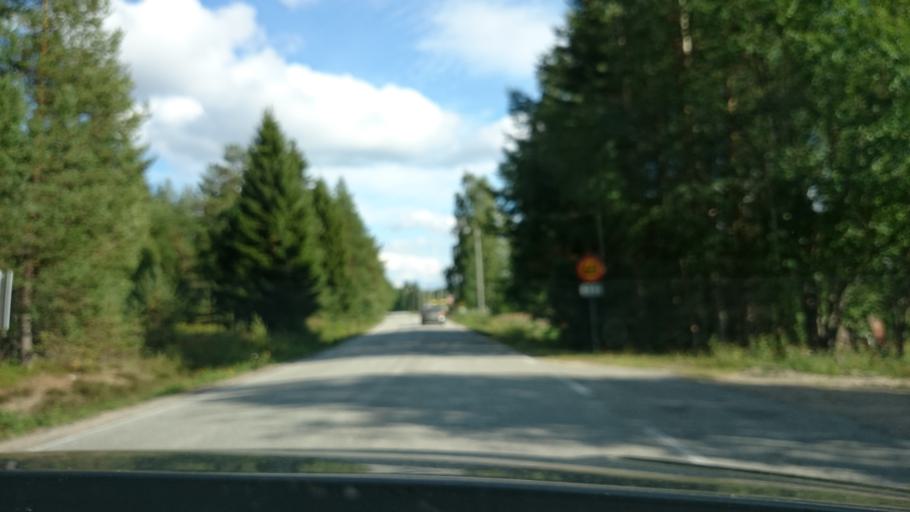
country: FI
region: Kainuu
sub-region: Kehys-Kainuu
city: Suomussalmi
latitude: 64.7469
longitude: 29.4416
